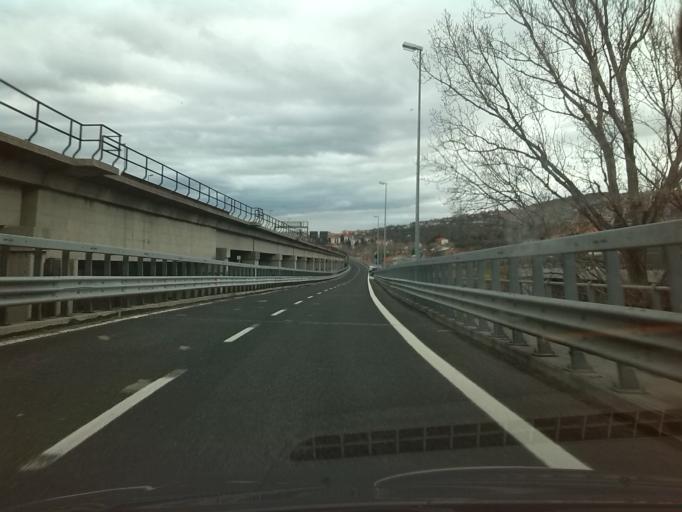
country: IT
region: Friuli Venezia Giulia
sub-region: Provincia di Trieste
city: Domio
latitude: 45.6093
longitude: 13.8302
